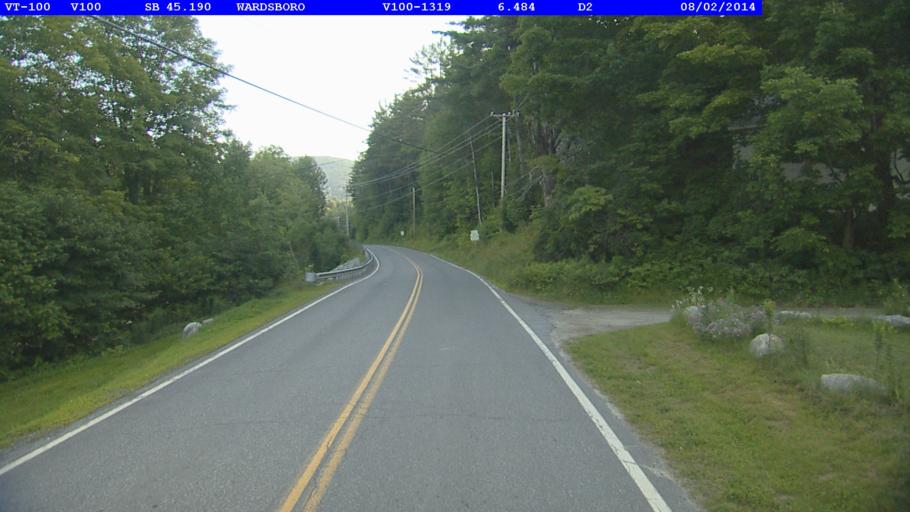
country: US
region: Vermont
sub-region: Windham County
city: Dover
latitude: 43.0403
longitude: -72.7905
